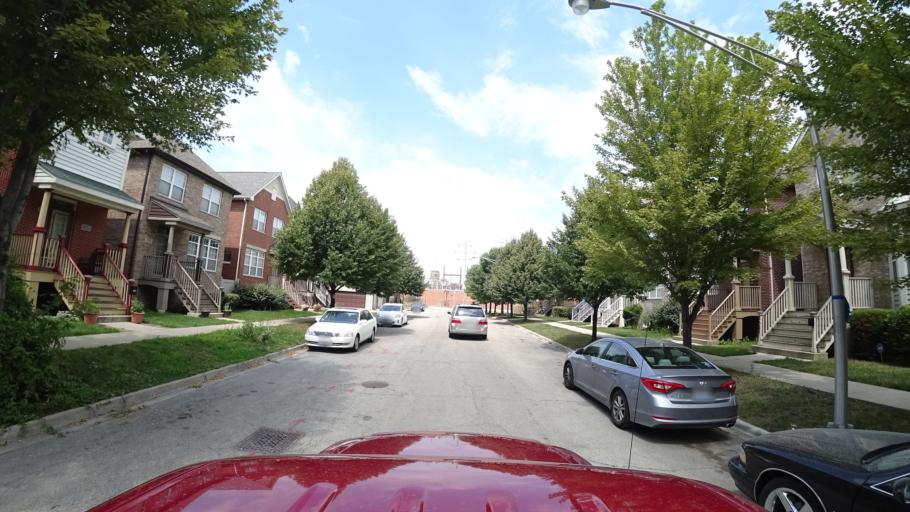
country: US
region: Illinois
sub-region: Cook County
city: Chicago
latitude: 41.8460
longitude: -87.6531
